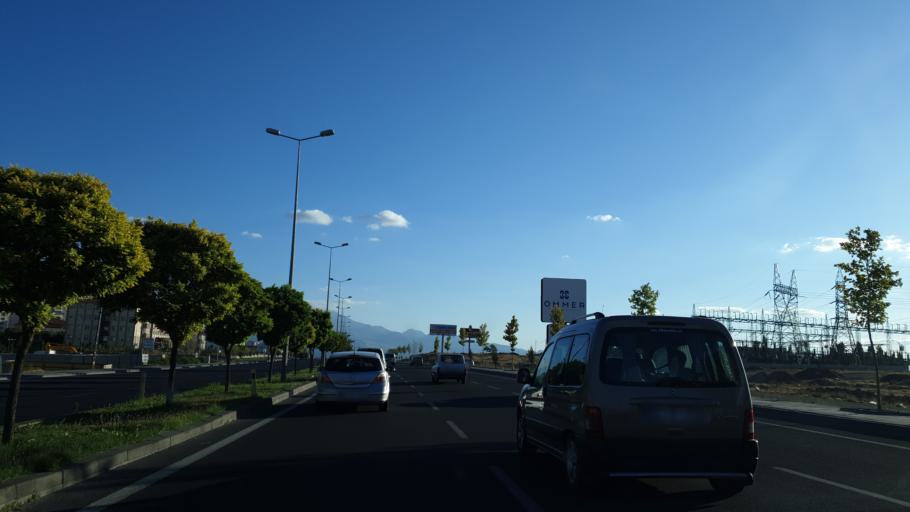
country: TR
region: Kayseri
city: Kocasinan
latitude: 38.7813
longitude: 35.5766
